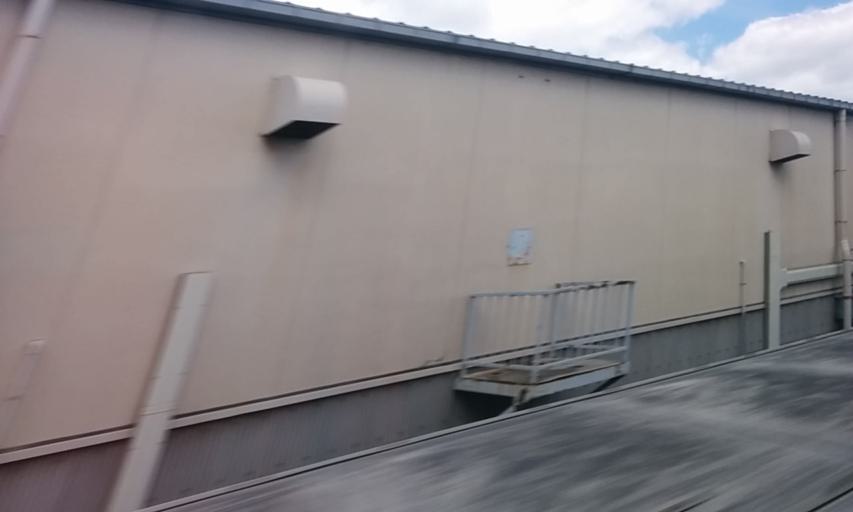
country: JP
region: Fukushima
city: Koriyama
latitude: 37.3851
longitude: 140.3855
